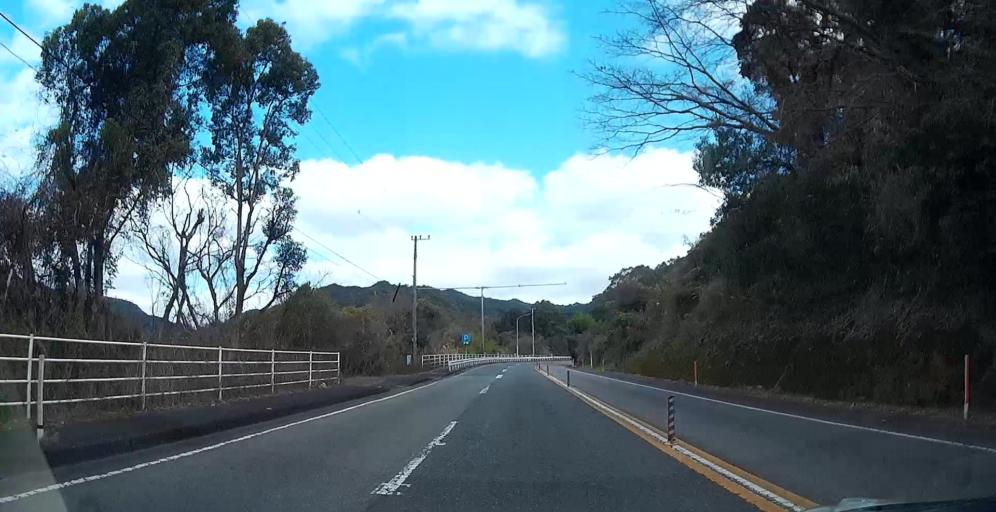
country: JP
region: Kumamoto
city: Yatsushiro
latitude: 32.3676
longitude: 130.5189
